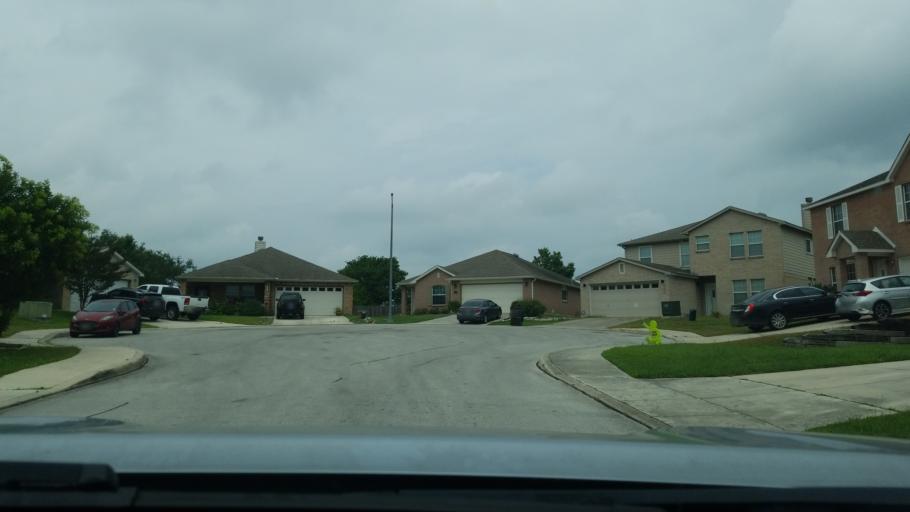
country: US
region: Texas
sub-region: Bexar County
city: Timberwood Park
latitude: 29.6819
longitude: -98.4622
